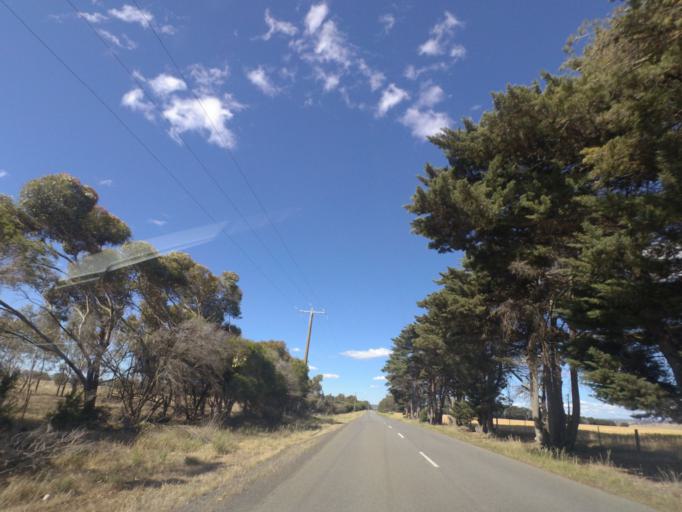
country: AU
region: Victoria
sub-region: Hume
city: Craigieburn
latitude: -37.4199
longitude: 144.8773
